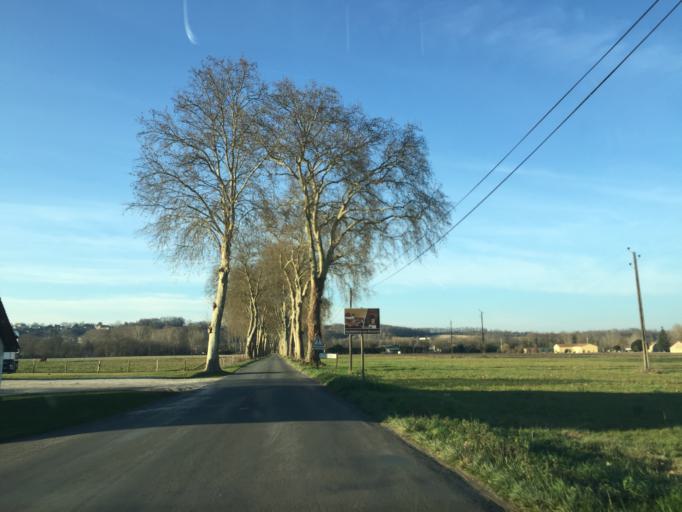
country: FR
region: Aquitaine
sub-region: Departement de la Dordogne
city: Saint-Aulaye
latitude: 45.2648
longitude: 0.1856
